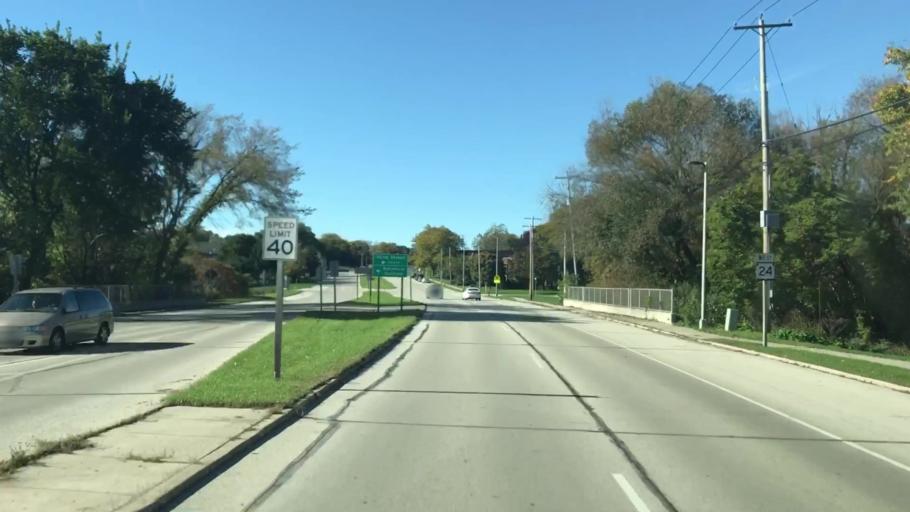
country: US
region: Wisconsin
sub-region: Milwaukee County
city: Greenfield
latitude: 42.9511
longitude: -88.0278
